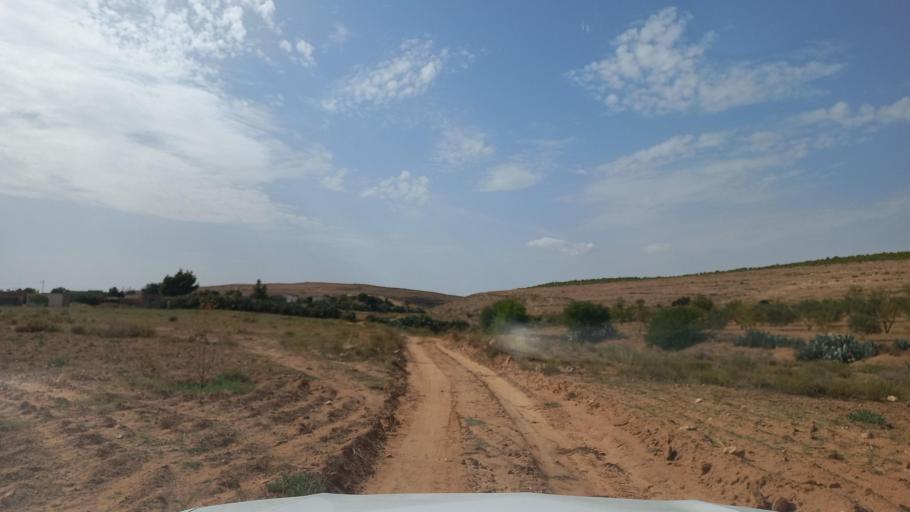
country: TN
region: Al Qasrayn
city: Kasserine
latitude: 35.3647
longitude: 8.8572
